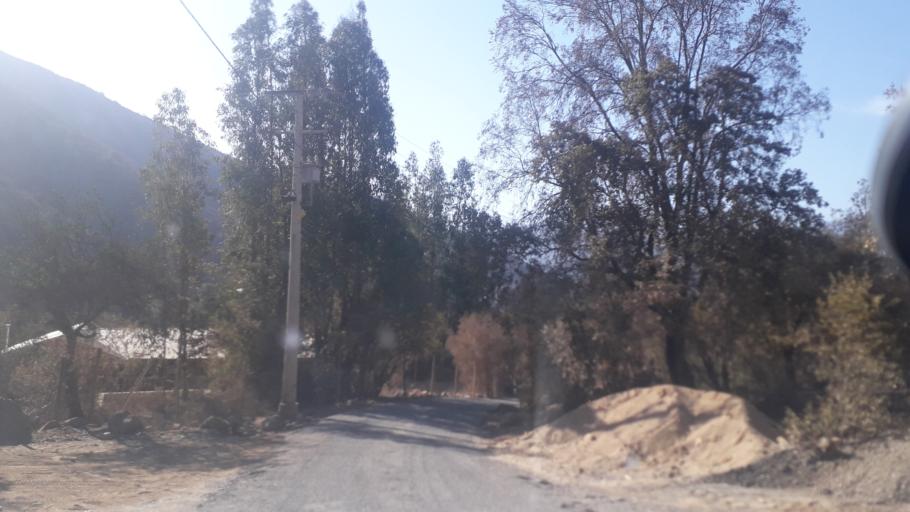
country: CL
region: Valparaiso
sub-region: Provincia de Marga Marga
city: Limache
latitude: -33.0806
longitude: -71.0999
